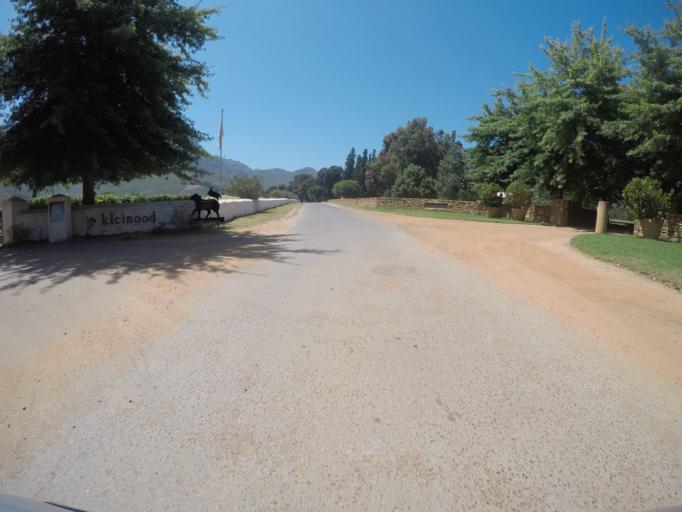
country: ZA
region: Western Cape
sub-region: Cape Winelands District Municipality
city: Stellenbosch
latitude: -33.9952
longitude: 18.8706
